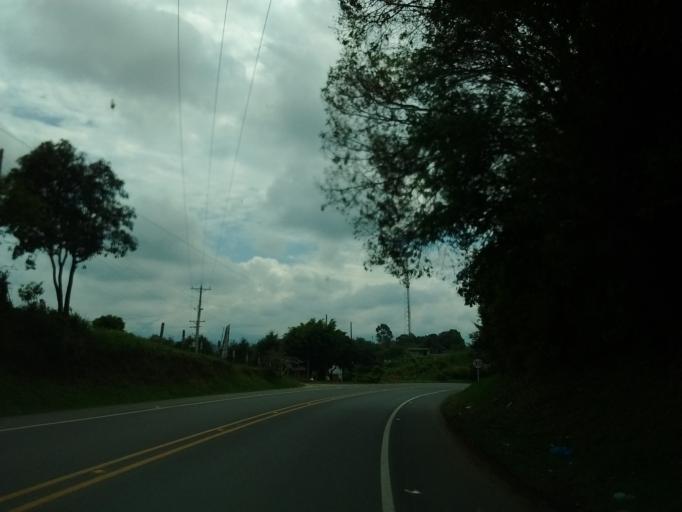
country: CO
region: Cauca
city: Cajibio
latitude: 2.5441
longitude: -76.5585
